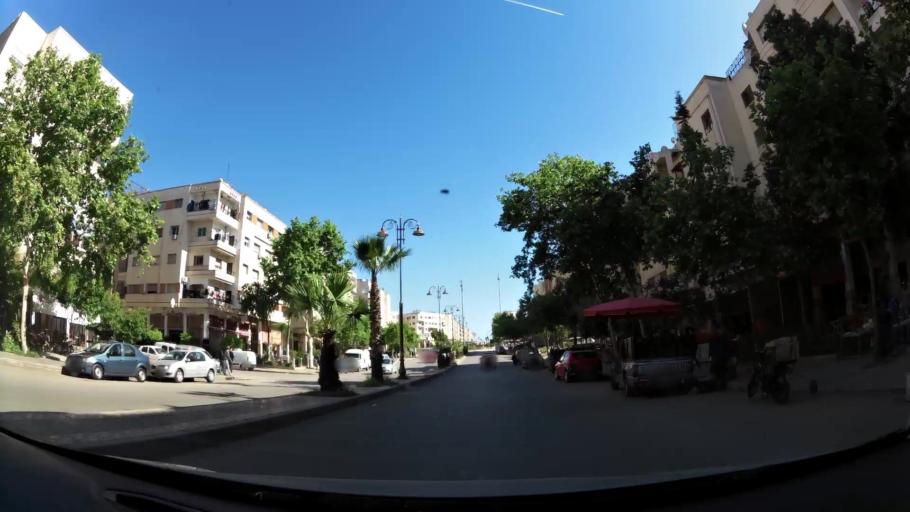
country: MA
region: Fes-Boulemane
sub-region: Fes
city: Fes
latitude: 34.0164
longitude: -4.9704
